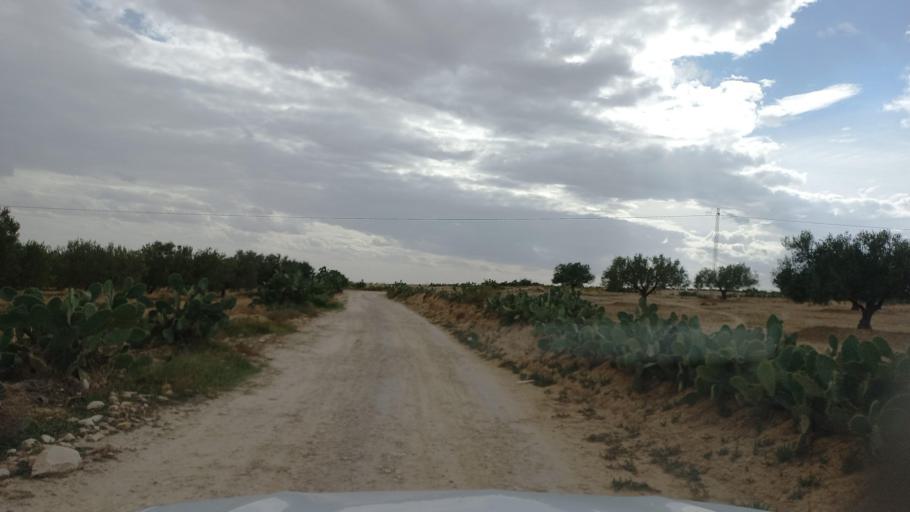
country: TN
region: Al Qasrayn
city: Sbiba
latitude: 35.4503
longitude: 9.0676
